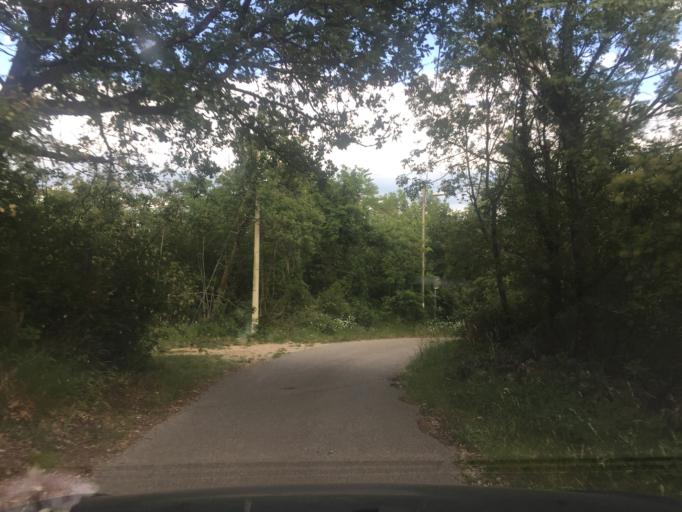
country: IT
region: Friuli Venezia Giulia
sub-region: Provincia di Gorizia
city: Savogna d'Isonzo
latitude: 45.8835
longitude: 13.5642
